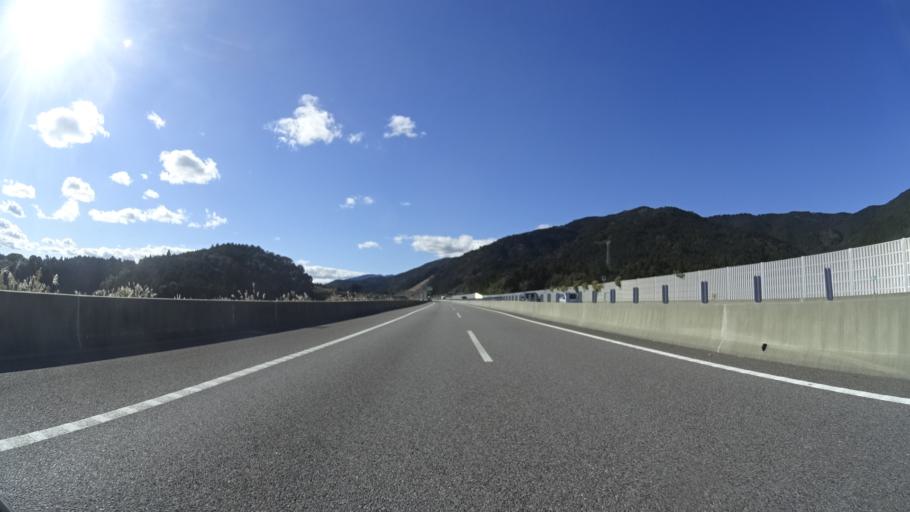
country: JP
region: Aichi
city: Shinshiro
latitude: 34.9272
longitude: 137.5189
